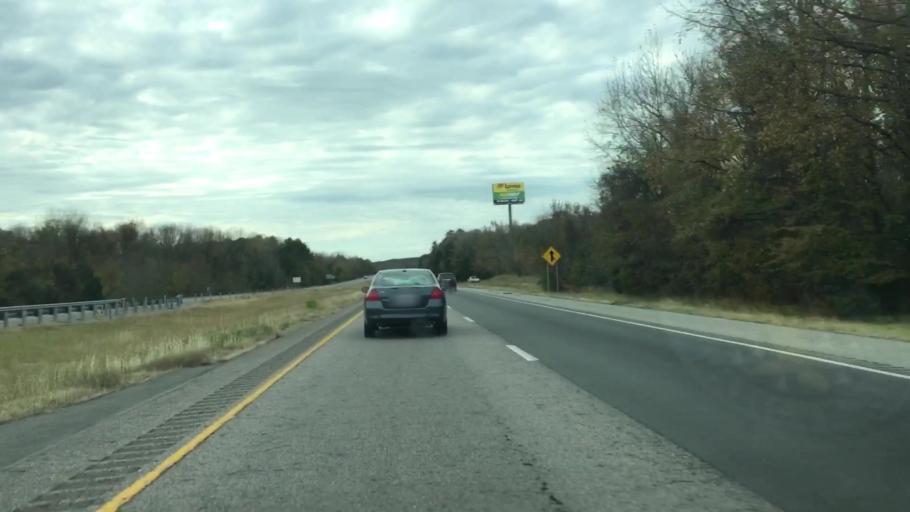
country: US
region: Arkansas
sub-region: Faulkner County
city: Conway
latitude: 35.1535
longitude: -92.5540
